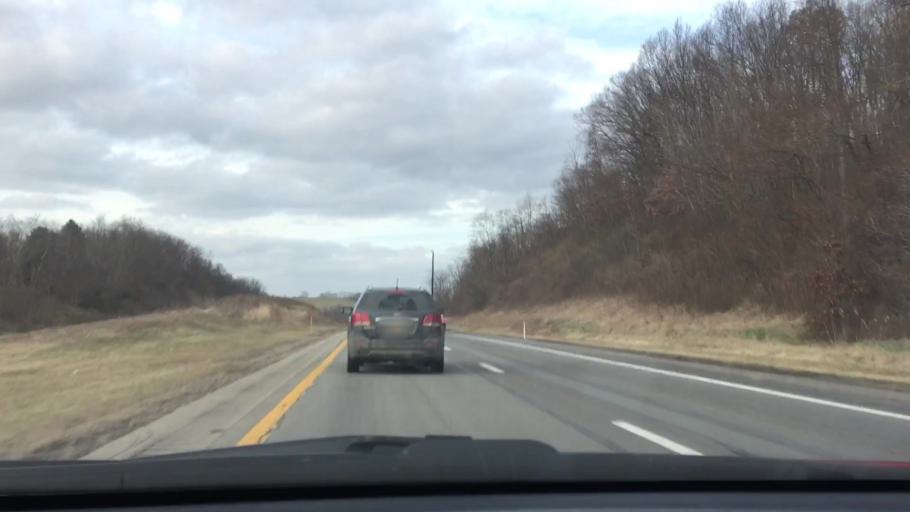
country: US
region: Pennsylvania
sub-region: Washington County
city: East Washington
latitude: 40.0739
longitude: -80.1902
